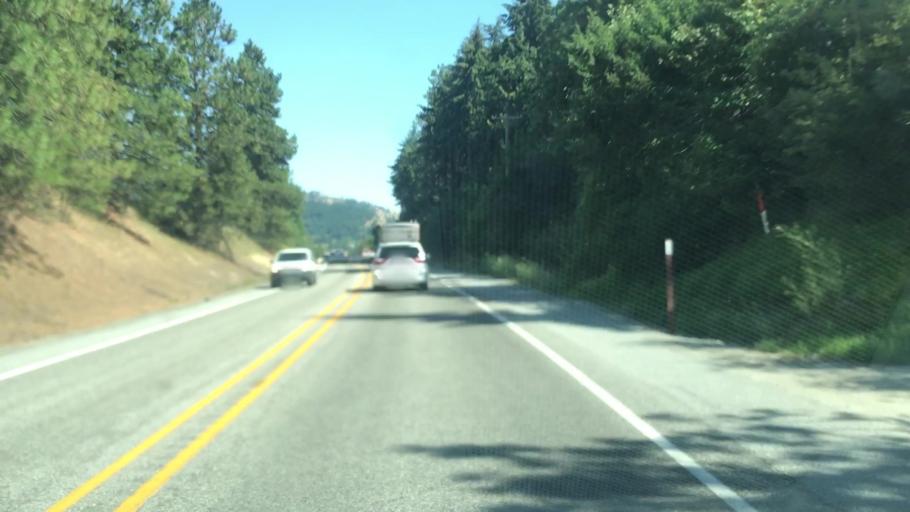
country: US
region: Washington
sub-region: Chelan County
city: Leavenworth
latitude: 47.5920
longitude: -120.6364
